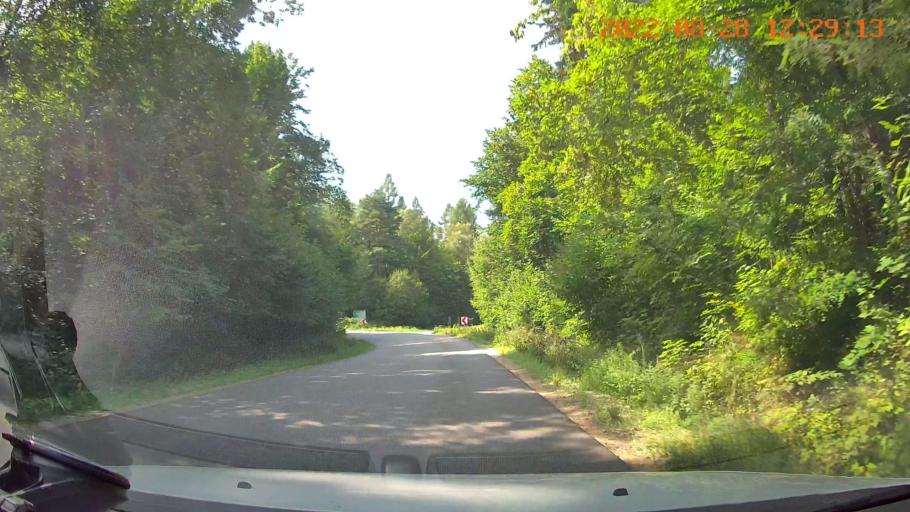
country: PL
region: Swietokrzyskie
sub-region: Powiat pinczowski
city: Michalow
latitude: 50.4178
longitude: 20.4674
